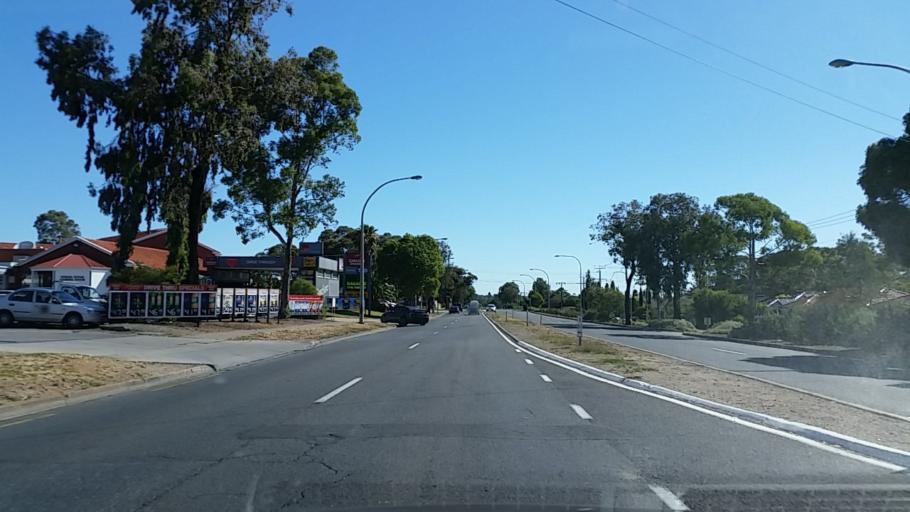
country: AU
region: South Australia
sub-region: Salisbury
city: Salisbury
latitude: -34.7995
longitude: 138.6558
